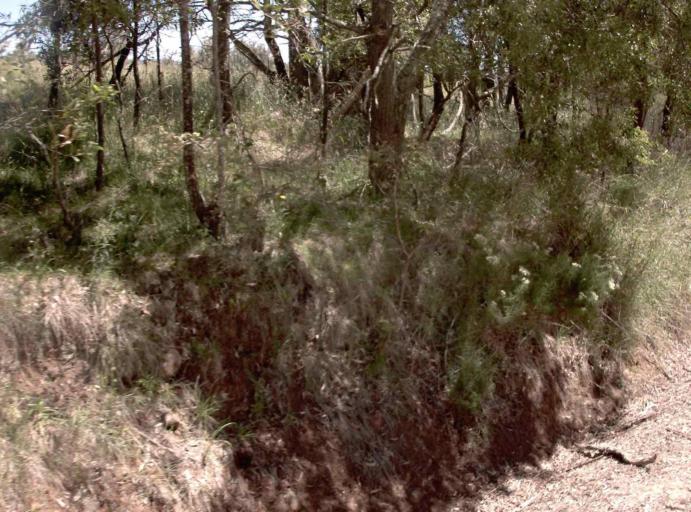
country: AU
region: Victoria
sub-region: East Gippsland
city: Lakes Entrance
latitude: -37.2439
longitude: 148.2558
